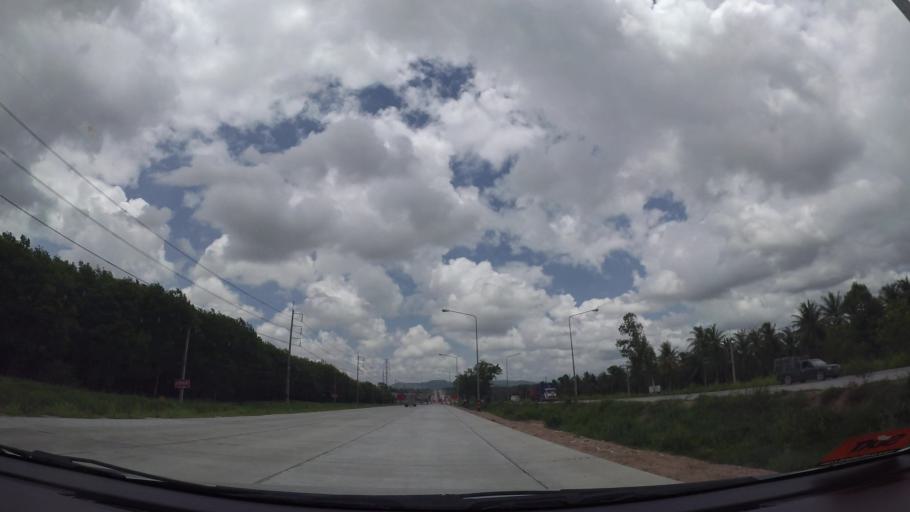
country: TH
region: Rayong
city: Ban Chang
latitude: 12.8907
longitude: 101.0471
